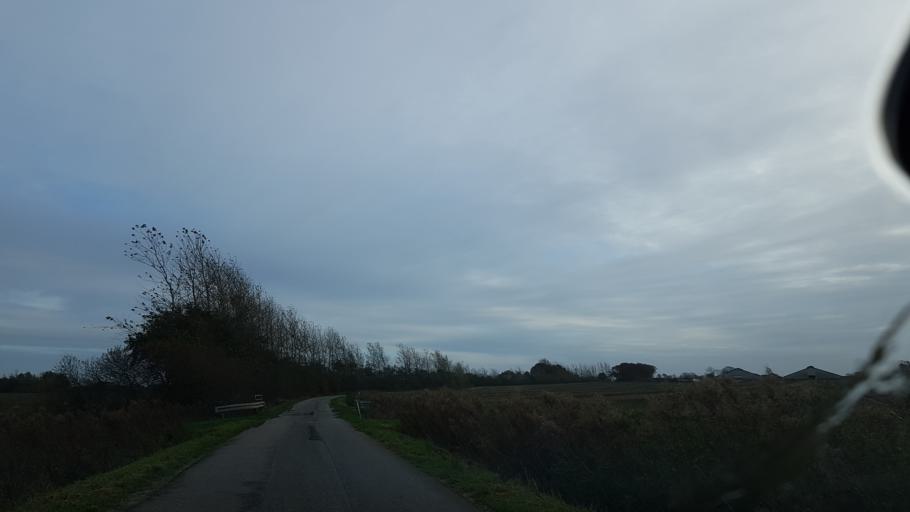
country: DK
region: South Denmark
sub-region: Tonder Kommune
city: Sherrebek
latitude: 55.2175
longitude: 8.8789
